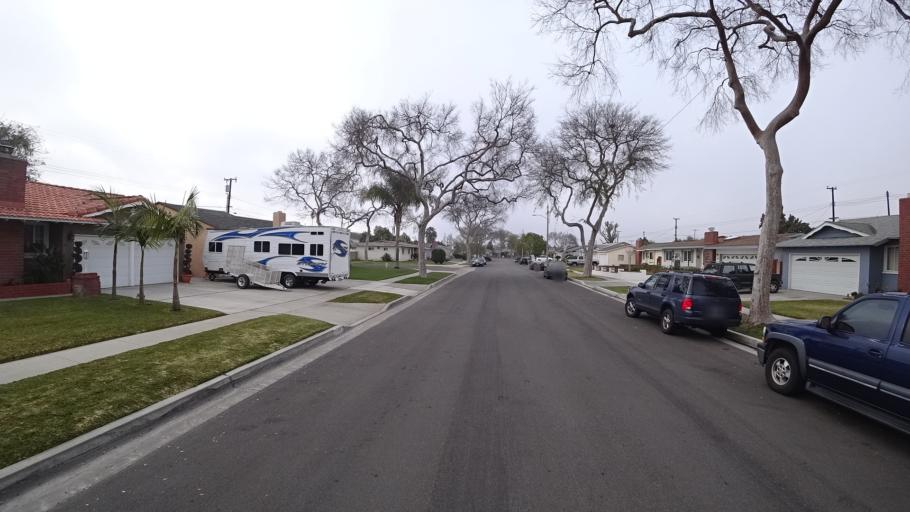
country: US
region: California
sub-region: Orange County
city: Stanton
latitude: 33.8156
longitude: -117.9981
